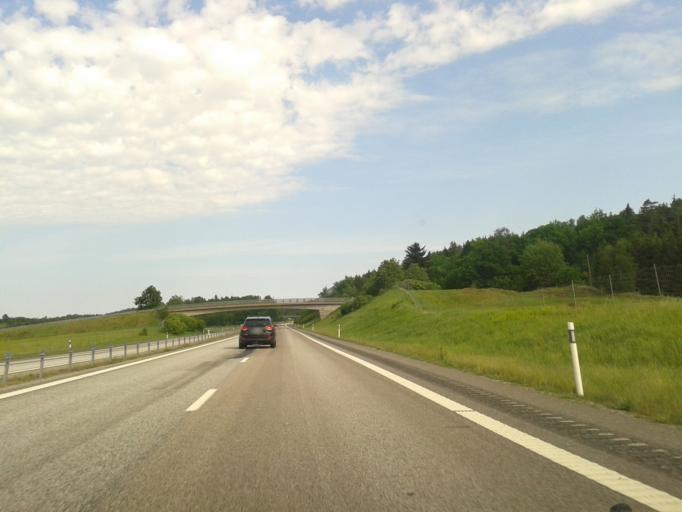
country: SE
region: Vaestra Goetaland
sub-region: Munkedals Kommun
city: Munkedal
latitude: 58.5345
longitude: 11.5336
